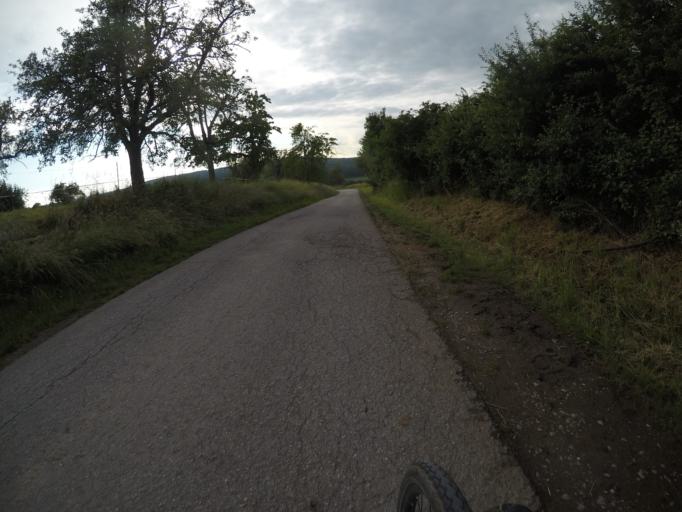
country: DE
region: Baden-Wuerttemberg
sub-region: Regierungsbezirk Stuttgart
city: Schlaitdorf
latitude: 48.6096
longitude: 9.2175
